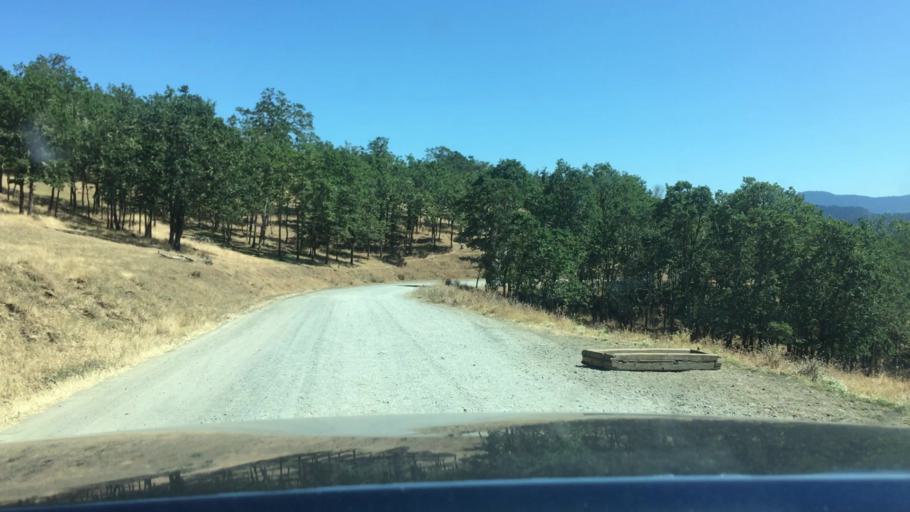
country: US
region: Oregon
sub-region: Douglas County
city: Winston
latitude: 43.1390
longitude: -123.4387
